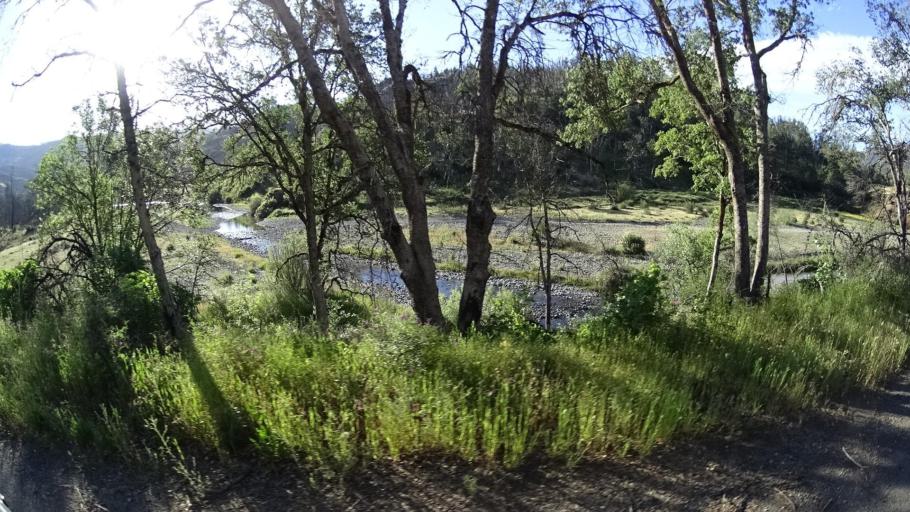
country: US
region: California
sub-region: Lake County
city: Upper Lake
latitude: 39.2550
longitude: -122.9493
